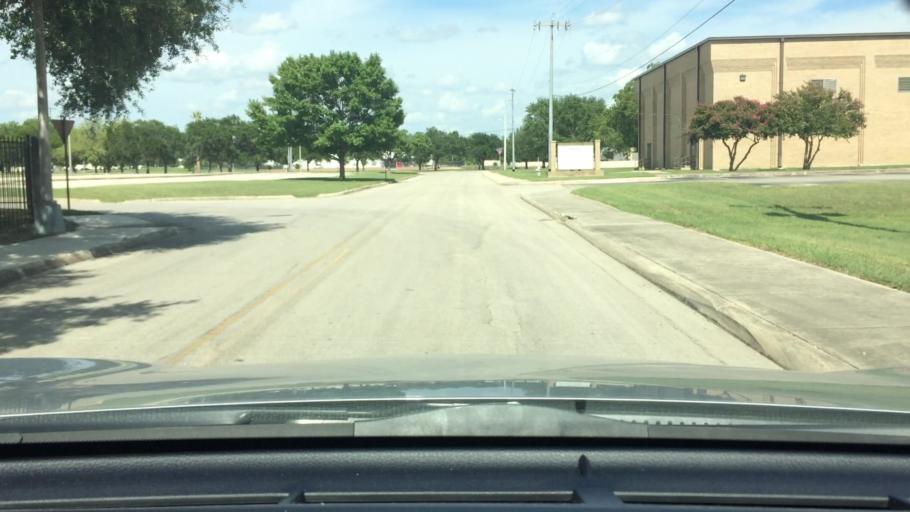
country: US
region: Texas
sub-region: Bexar County
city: San Antonio
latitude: 29.3416
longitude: -98.4473
